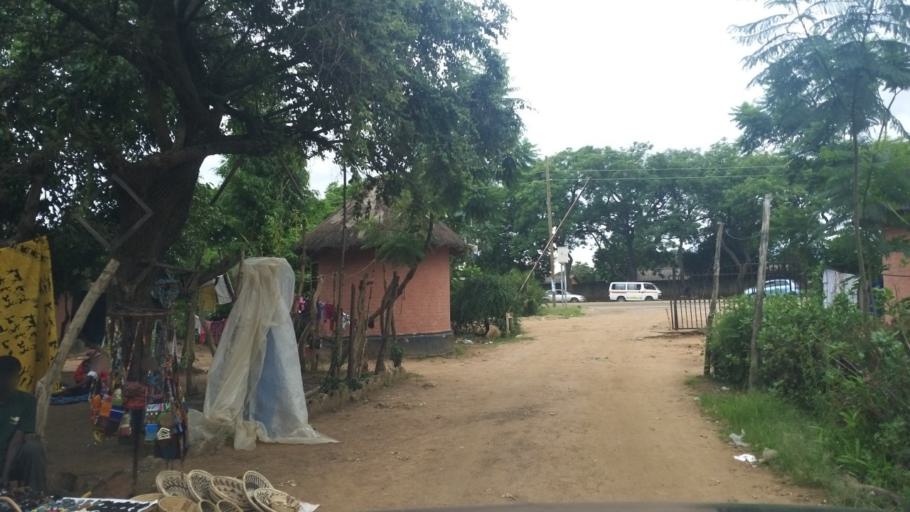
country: ZM
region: Lusaka
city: Lusaka
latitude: -15.4324
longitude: 28.3049
